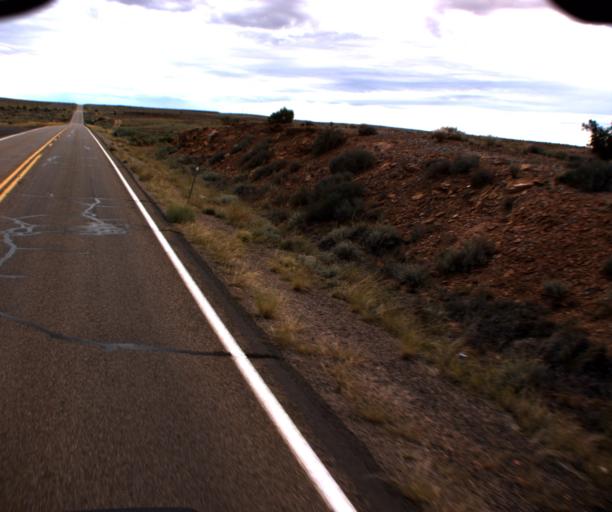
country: US
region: Arizona
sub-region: Navajo County
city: Holbrook
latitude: 34.8420
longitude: -110.1465
